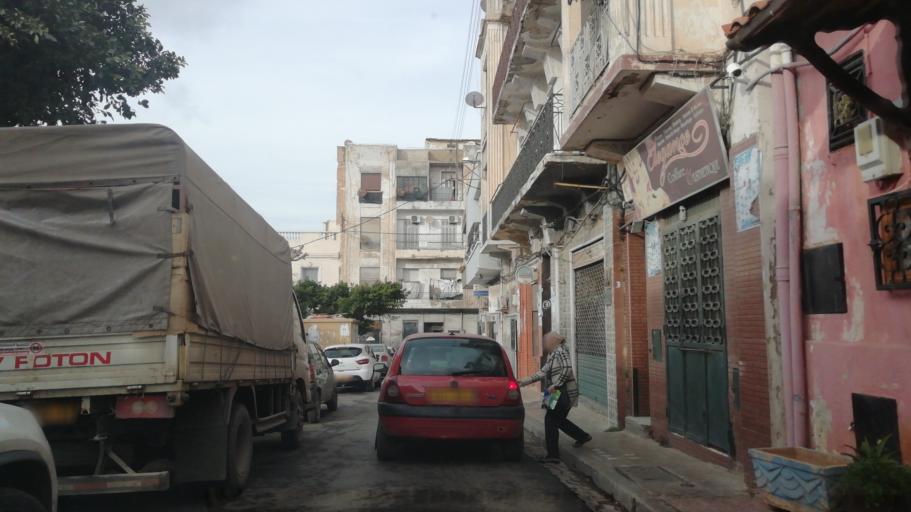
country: DZ
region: Oran
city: Oran
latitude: 35.6993
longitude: -0.6249
